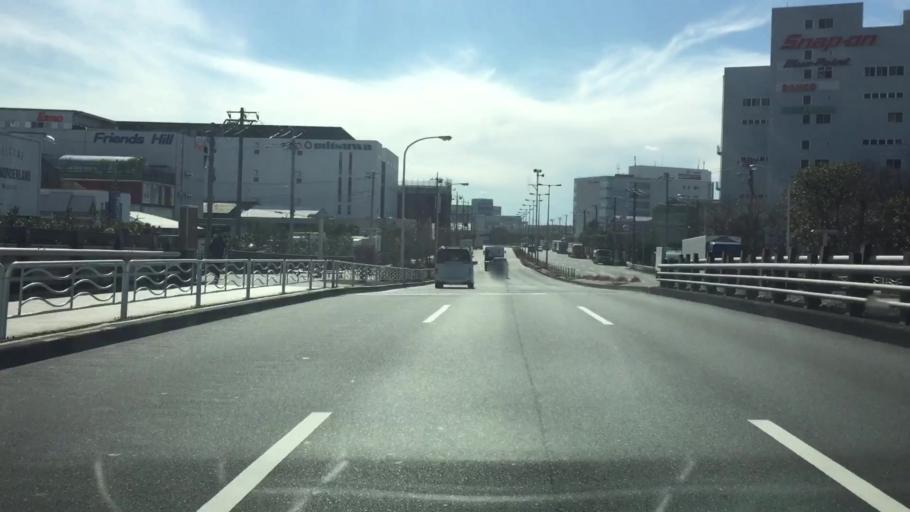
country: JP
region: Tokyo
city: Urayasu
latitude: 35.6426
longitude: 139.8246
